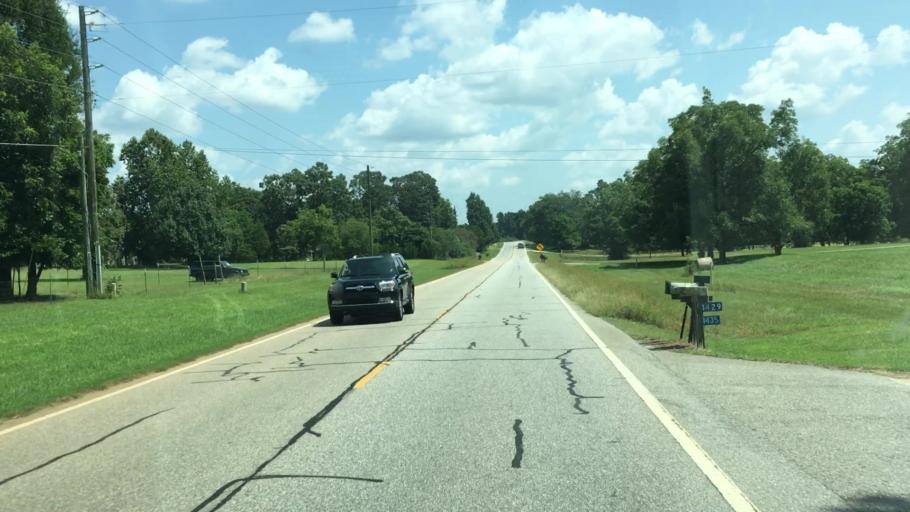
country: US
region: Georgia
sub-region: Barrow County
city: Statham
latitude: 33.9407
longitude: -83.6397
